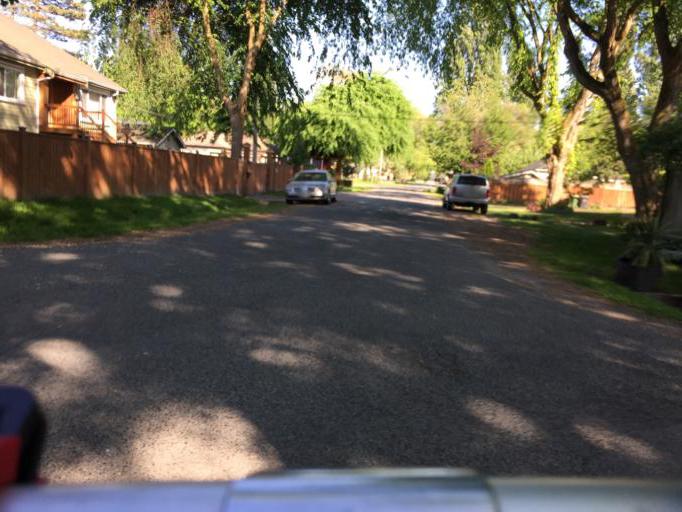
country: CA
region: British Columbia
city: Richmond
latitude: 49.1883
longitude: -123.1485
